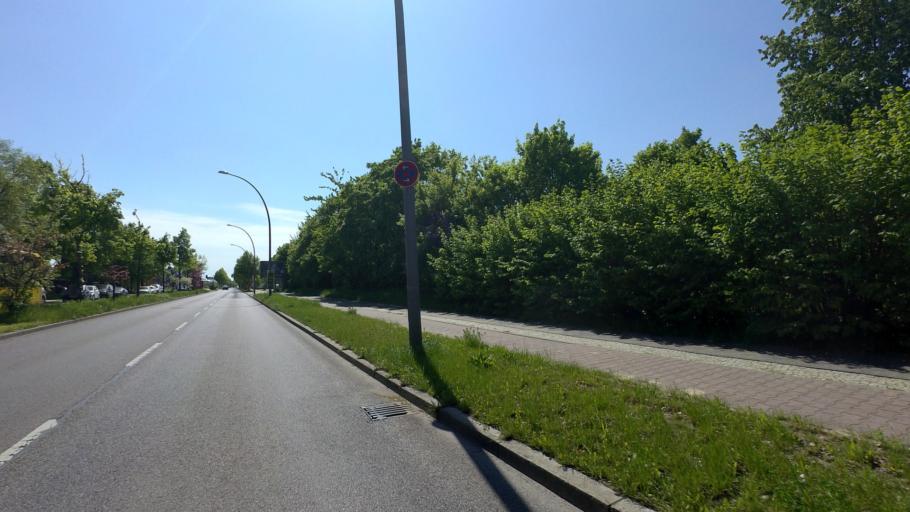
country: DE
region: Brandenburg
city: Schonefeld
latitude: 52.4020
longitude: 13.5130
